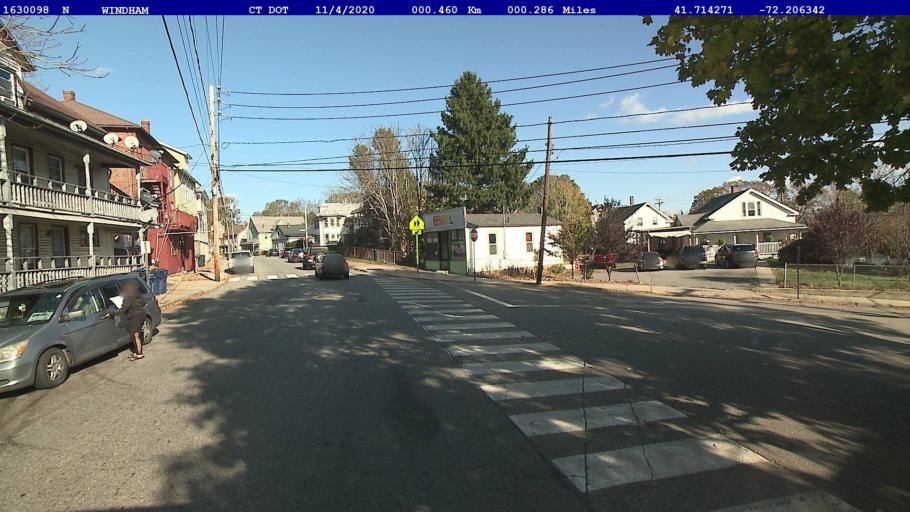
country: US
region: Connecticut
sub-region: Windham County
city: Willimantic
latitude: 41.7143
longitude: -72.2063
